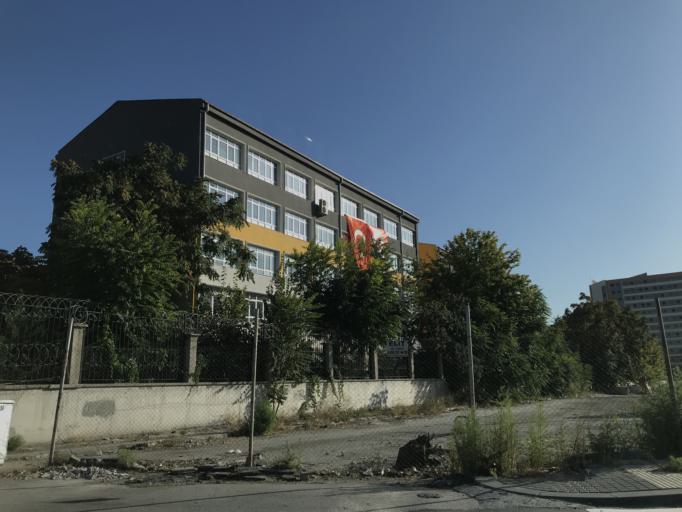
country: TR
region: Ankara
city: Ankara
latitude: 39.9519
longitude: 32.8514
